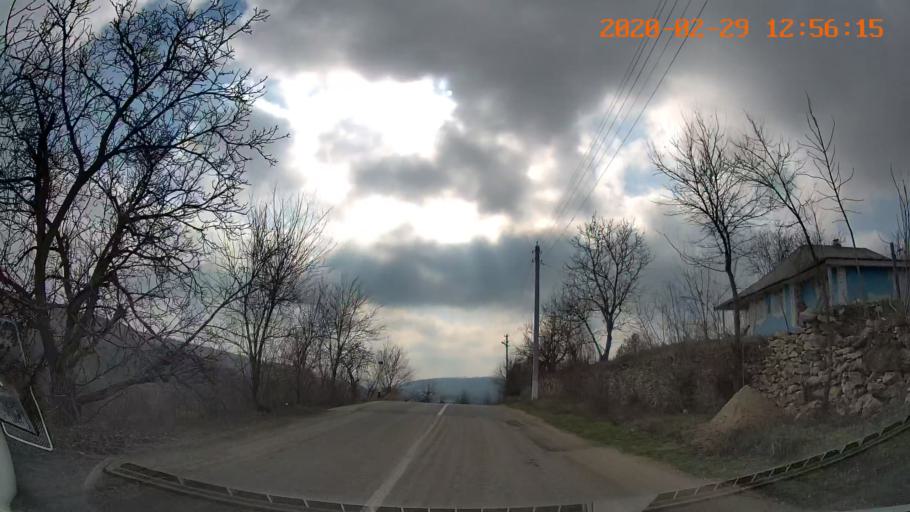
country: MD
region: Telenesti
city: Camenca
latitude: 48.0885
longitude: 28.7228
